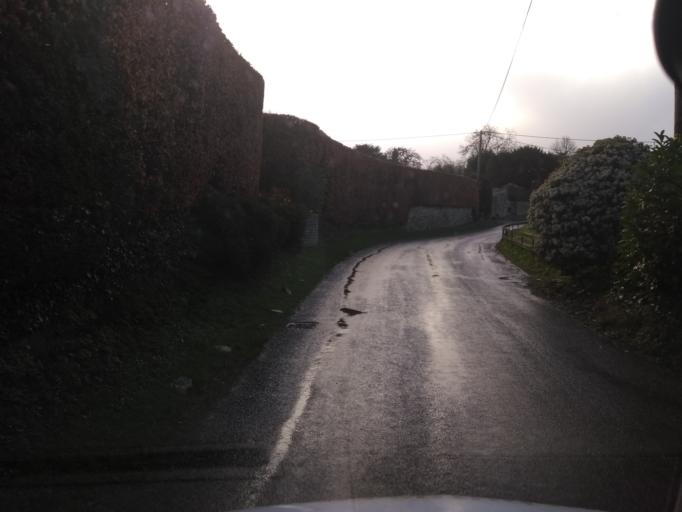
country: GB
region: England
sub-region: Dorset
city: Sherborne
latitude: 50.9953
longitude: -2.5586
